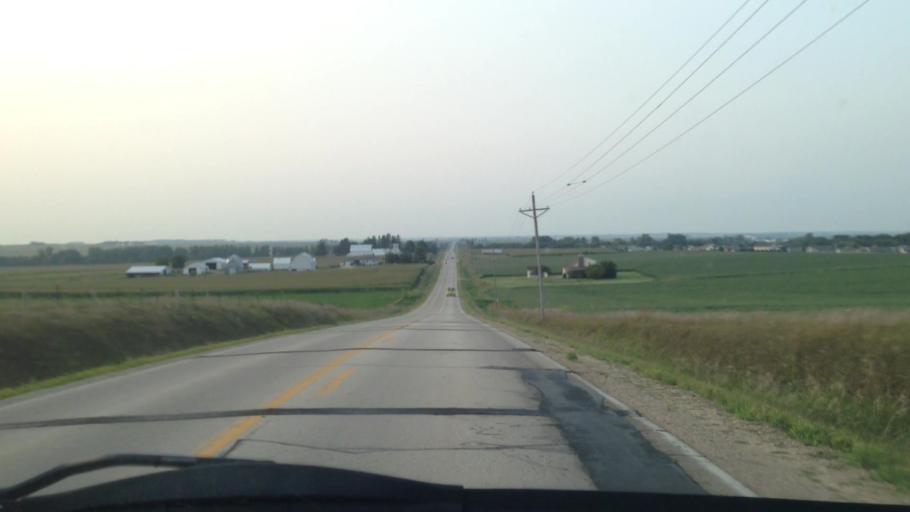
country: US
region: Iowa
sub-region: Benton County
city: Atkins
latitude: 41.9862
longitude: -91.8731
